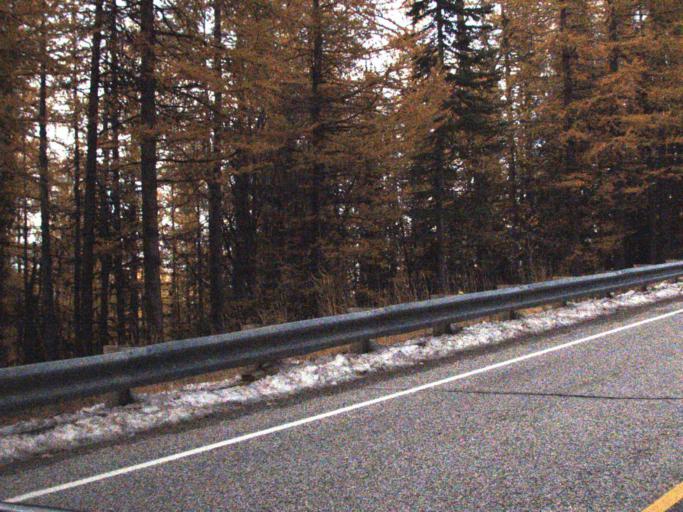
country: US
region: Washington
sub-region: Ferry County
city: Republic
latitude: 48.6066
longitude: -118.4605
